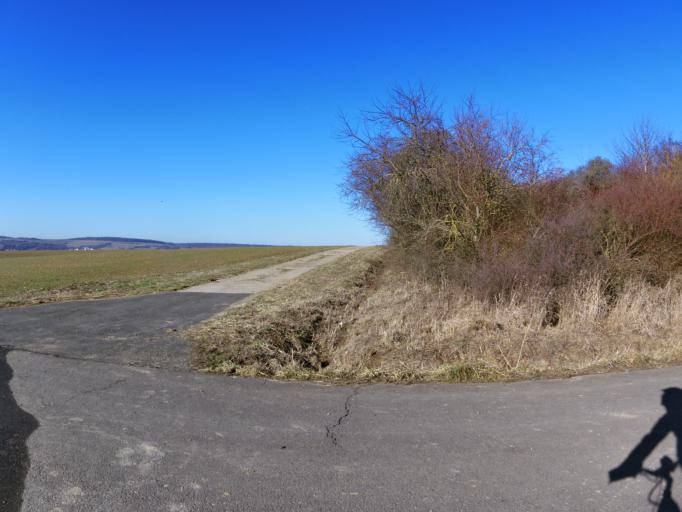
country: DE
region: Bavaria
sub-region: Regierungsbezirk Unterfranken
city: Estenfeld
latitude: 49.8437
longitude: 9.9831
